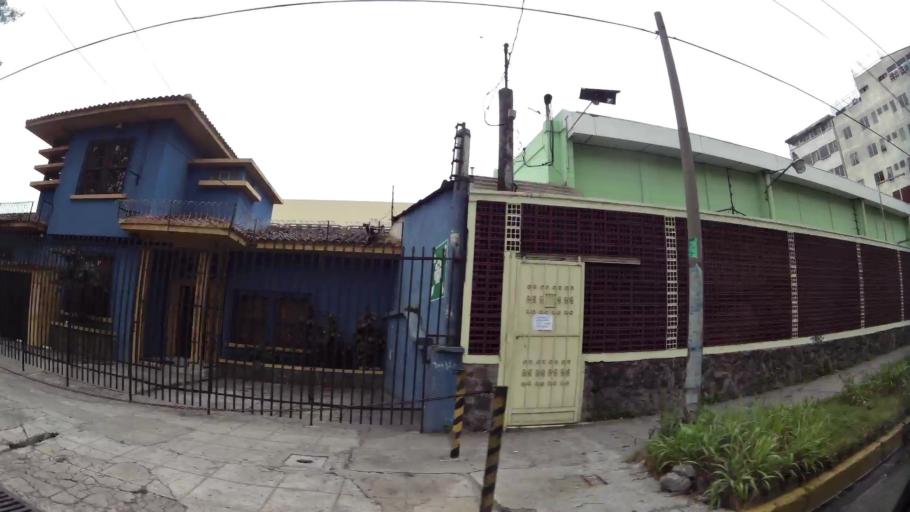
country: SV
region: San Salvador
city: San Salvador
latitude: 13.7011
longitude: -89.2030
